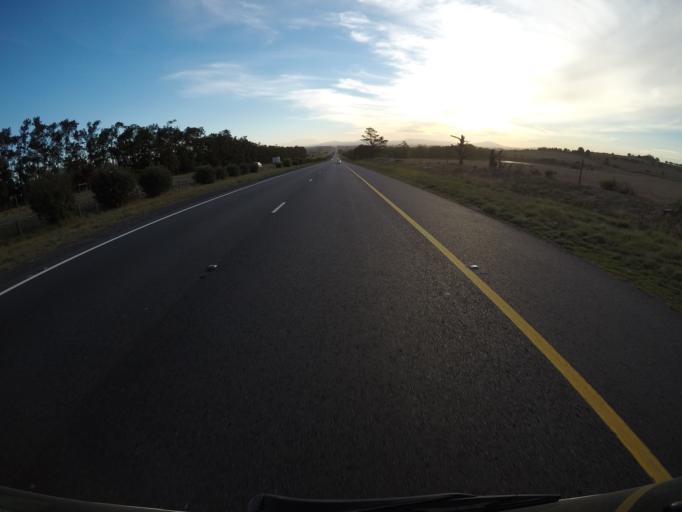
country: ZA
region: Western Cape
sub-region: City of Cape Town
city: Kraaifontein
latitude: -33.8115
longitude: 18.8210
